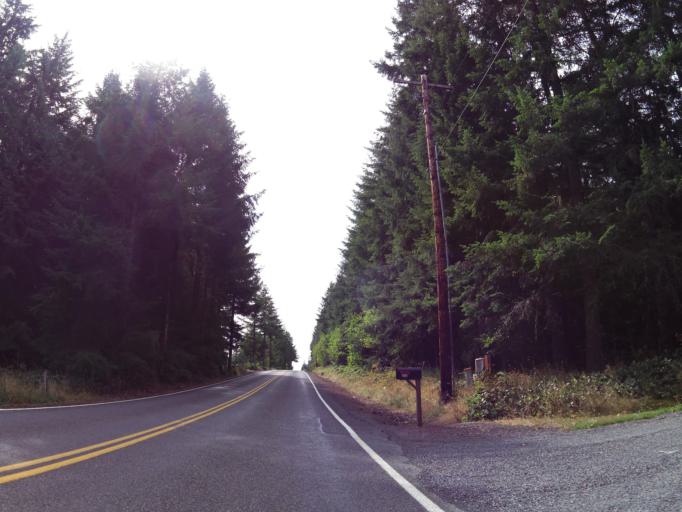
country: US
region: Washington
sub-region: Lewis County
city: Chehalis
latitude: 46.6042
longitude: -122.9712
